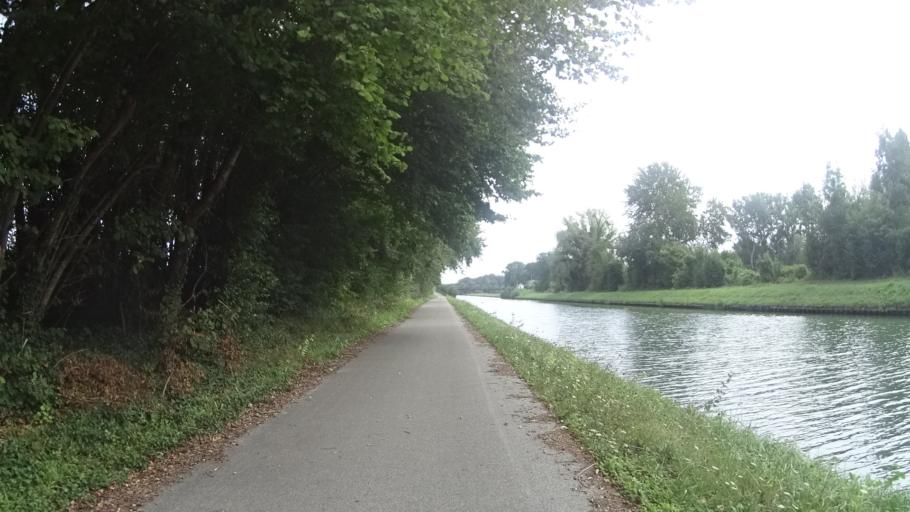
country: FR
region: Picardie
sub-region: Departement de l'Oise
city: Crisolles
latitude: 49.5778
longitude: 3.0784
